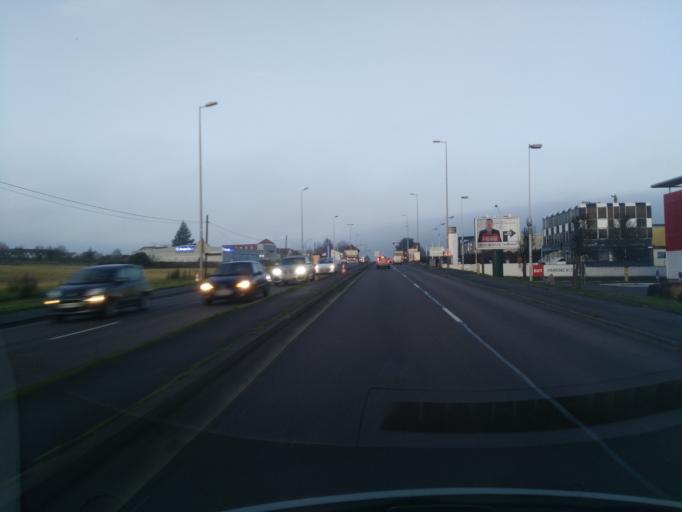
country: FR
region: Ile-de-France
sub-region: Departement des Yvelines
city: Orgeval
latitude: 48.9275
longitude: 1.9847
